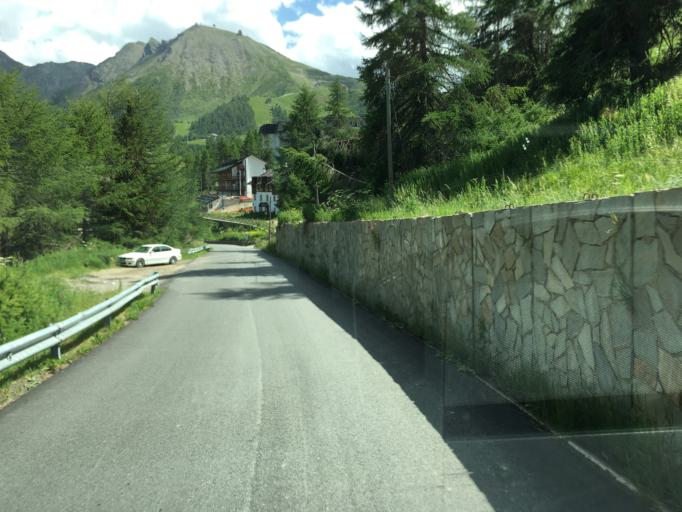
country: IT
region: Piedmont
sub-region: Provincia di Torino
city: Sestriere
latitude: 44.9633
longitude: 6.8826
